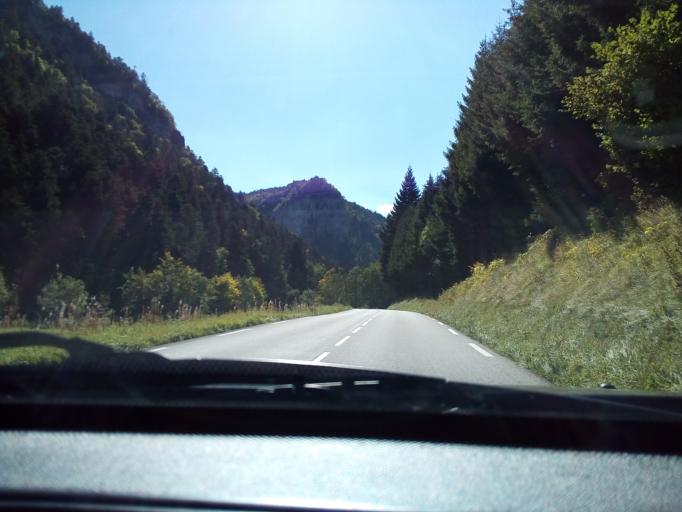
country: FR
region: Rhone-Alpes
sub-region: Departement de l'Isere
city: Lans-en-Vercors
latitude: 45.1591
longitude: 5.6082
